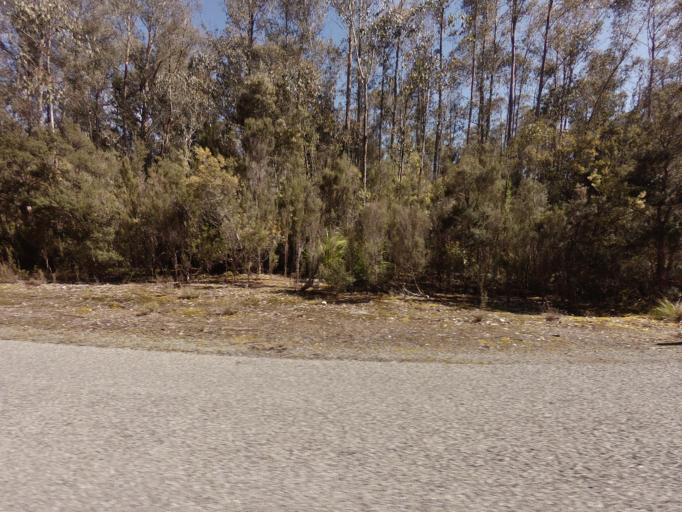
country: AU
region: Tasmania
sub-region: Derwent Valley
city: New Norfolk
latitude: -42.7579
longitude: 146.4067
